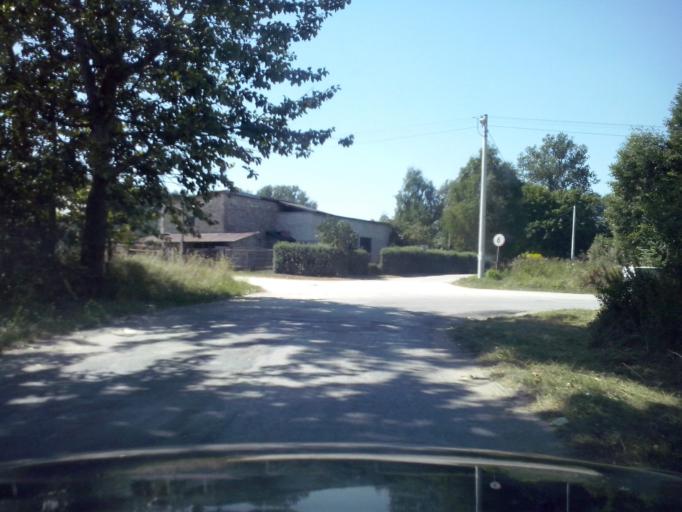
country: PL
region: Swietokrzyskie
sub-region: Powiat kielecki
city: Chmielnik
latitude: 50.6053
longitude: 20.7817
